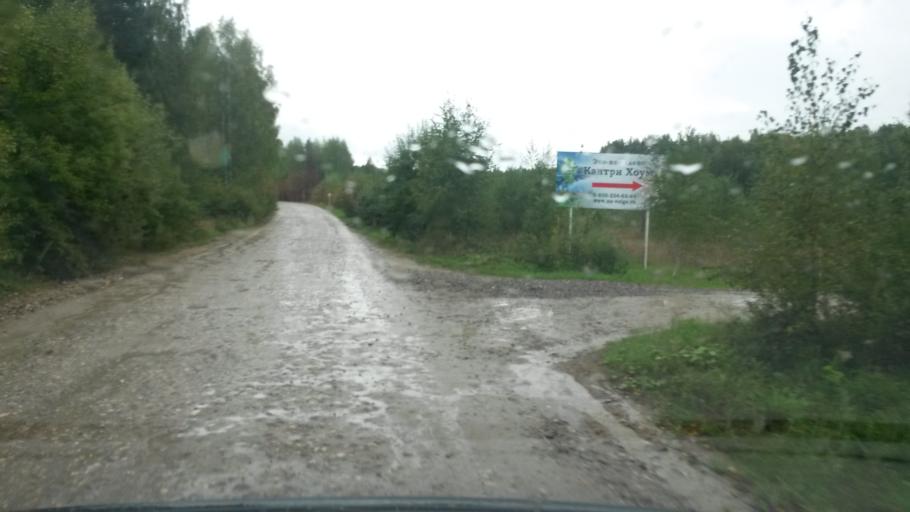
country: RU
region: Ivanovo
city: Zarechnyy
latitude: 57.5025
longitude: 42.2905
